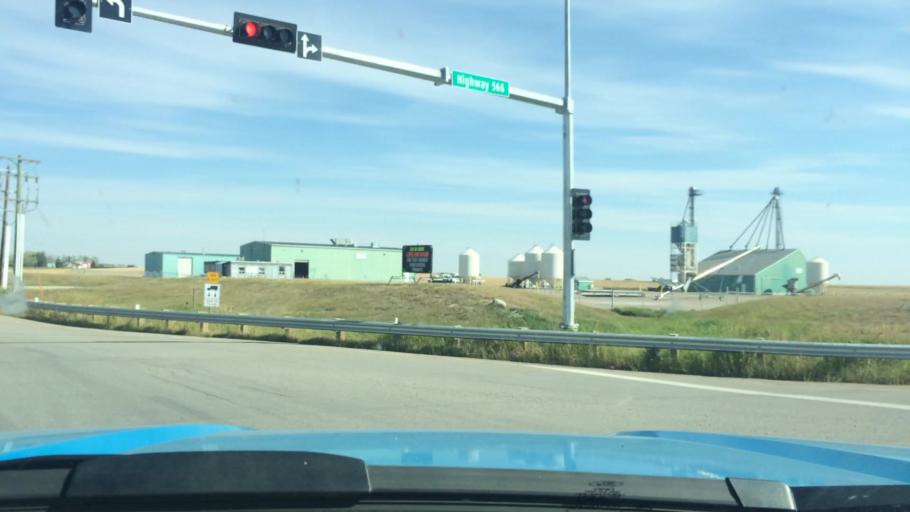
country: CA
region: Alberta
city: Airdrie
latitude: 51.2127
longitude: -113.9352
